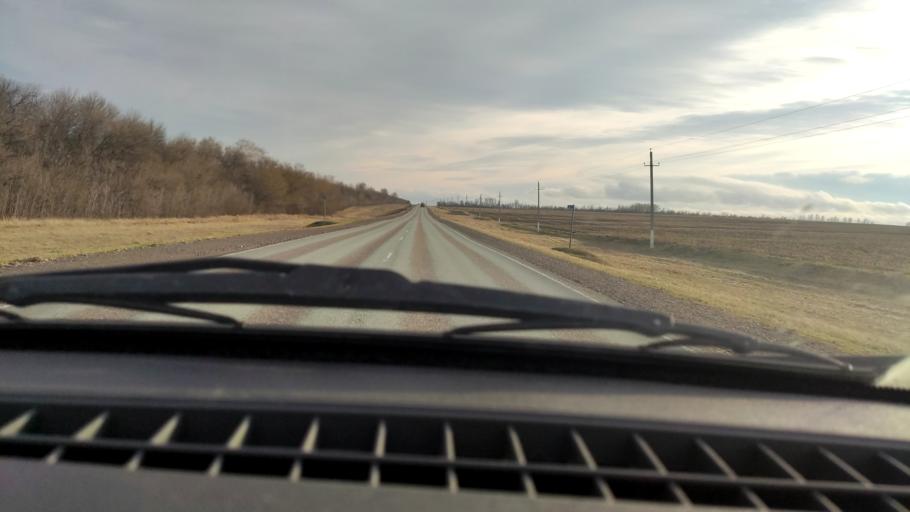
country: RU
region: Bashkortostan
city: Davlekanovo
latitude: 54.3272
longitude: 55.1632
